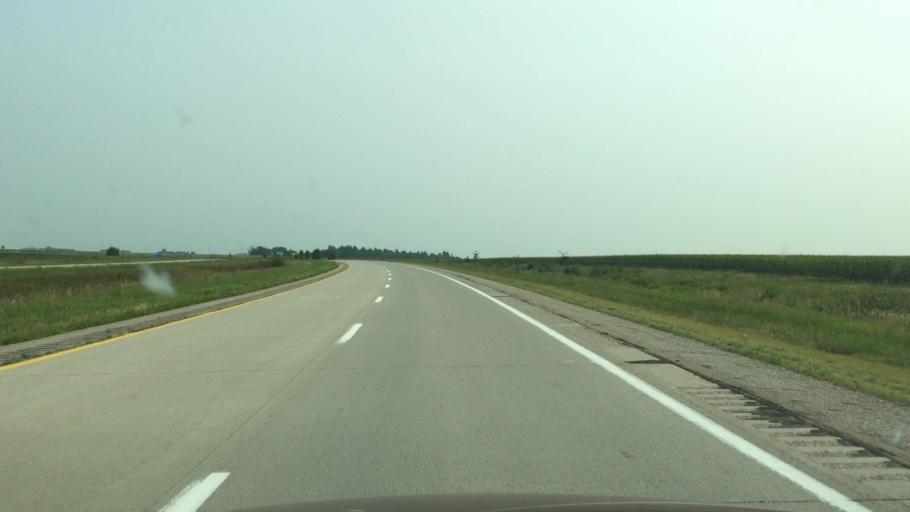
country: US
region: Iowa
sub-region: Osceola County
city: Sibley
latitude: 43.3902
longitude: -95.7193
